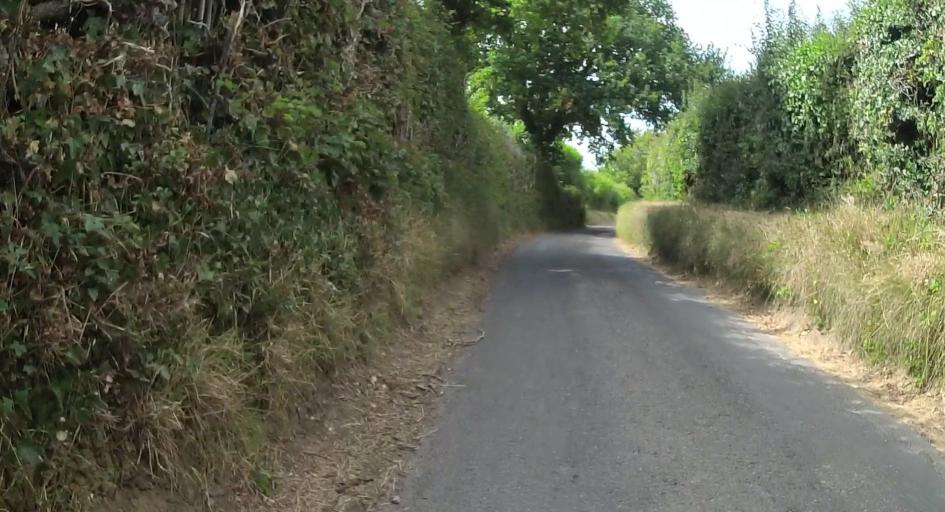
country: GB
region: England
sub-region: Dorset
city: Swanage
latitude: 50.6242
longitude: -1.9901
